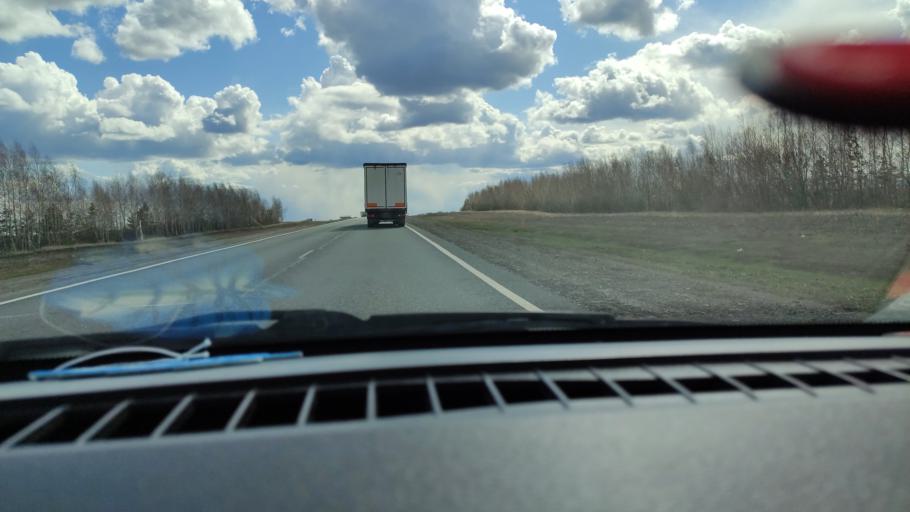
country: RU
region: Saratov
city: Dukhovnitskoye
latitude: 52.8114
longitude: 48.2295
